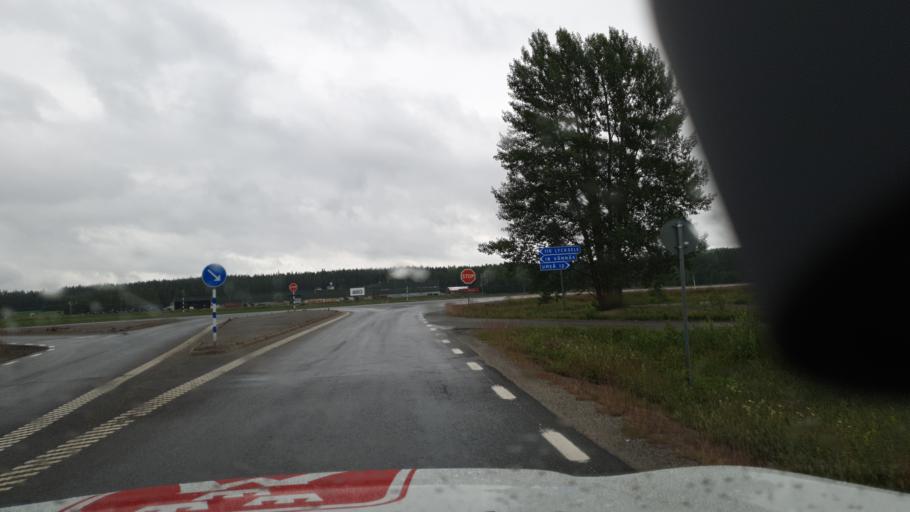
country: SE
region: Vaesterbotten
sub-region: Umea Kommun
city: Roback
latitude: 63.8746
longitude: 20.0613
